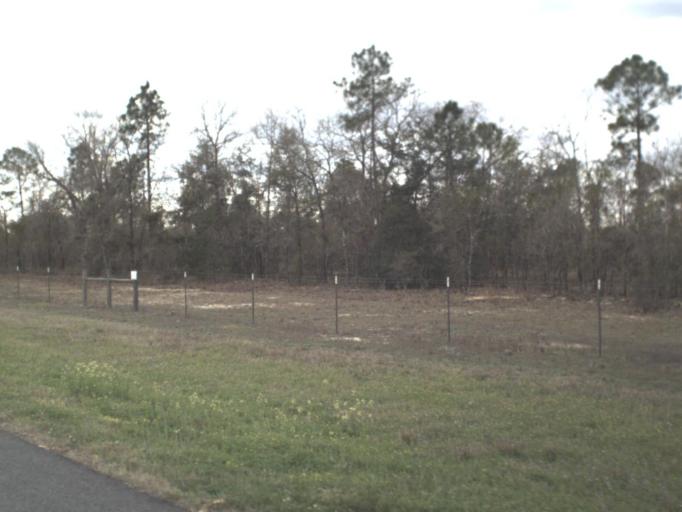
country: US
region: Florida
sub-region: Gadsden County
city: Quincy
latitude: 30.4602
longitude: -84.6401
